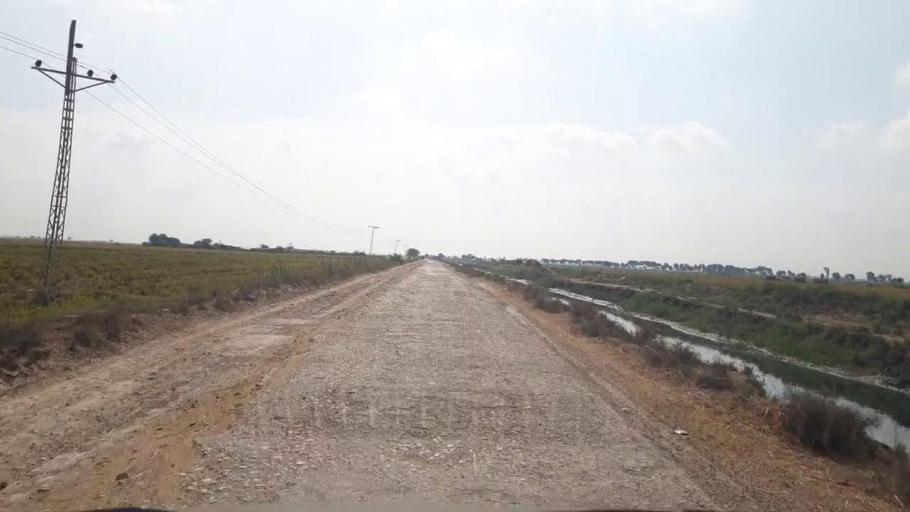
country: PK
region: Sindh
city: Kario
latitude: 24.6312
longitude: 68.5507
